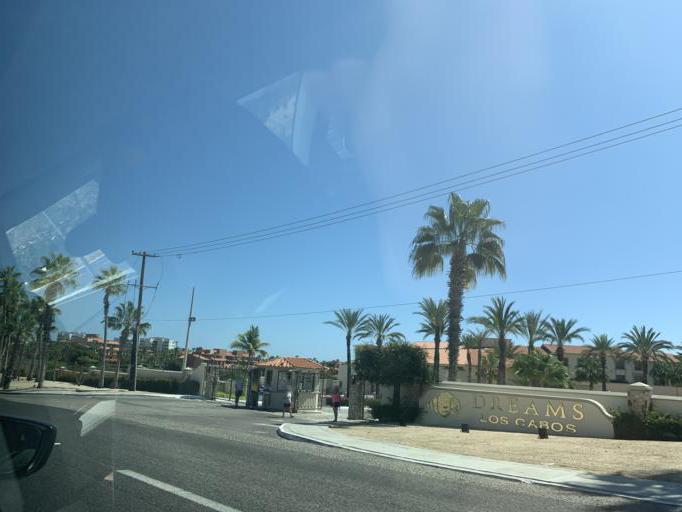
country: MX
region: Baja California Sur
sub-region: Los Cabos
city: San Jose del Cabo
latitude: 22.9768
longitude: -109.7776
